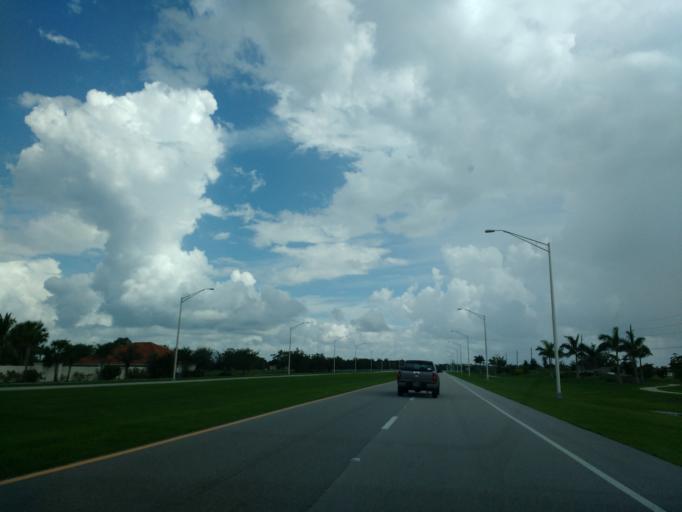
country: US
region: Florida
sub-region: Lee County
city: Burnt Store Marina
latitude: 26.7898
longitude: -82.0379
